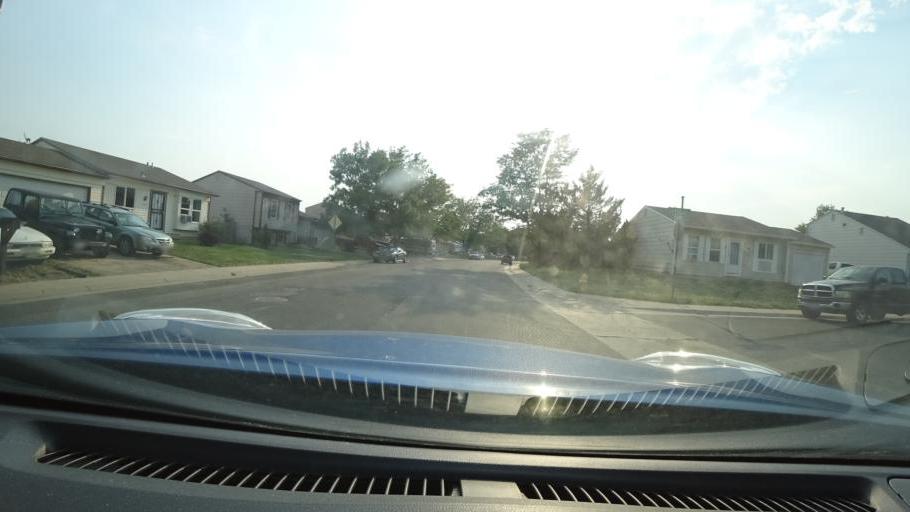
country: US
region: Colorado
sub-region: Adams County
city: Aurora
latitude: 39.7420
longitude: -104.7551
